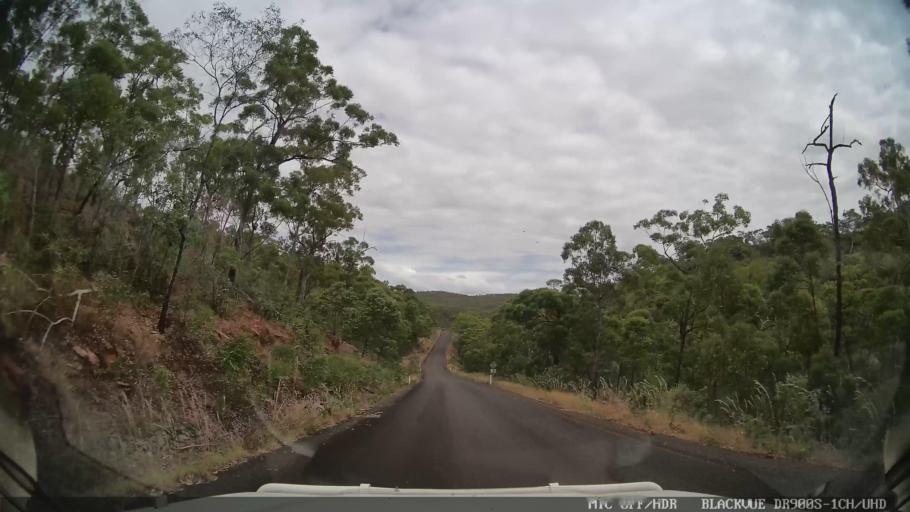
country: AU
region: Queensland
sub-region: Cook
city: Cooktown
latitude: -15.2830
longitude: 144.9067
